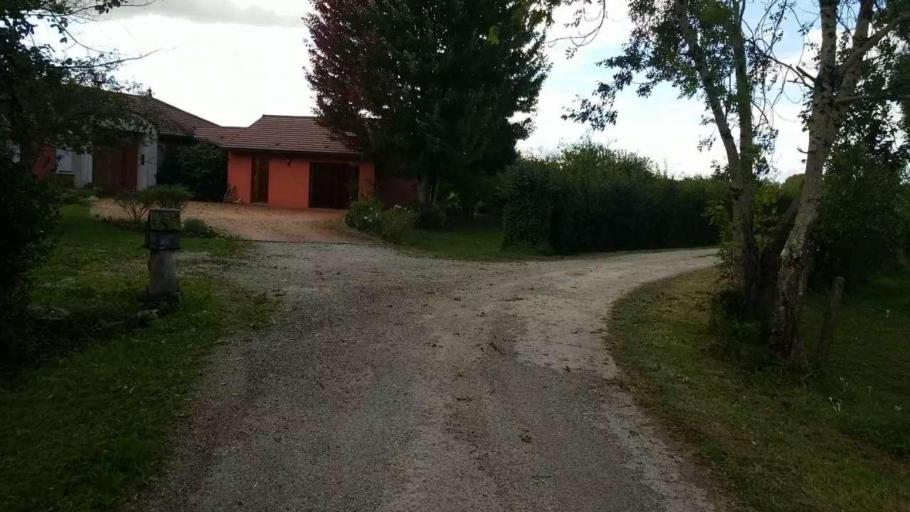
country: FR
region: Franche-Comte
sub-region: Departement du Jura
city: Bletterans
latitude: 46.7486
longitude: 5.4405
